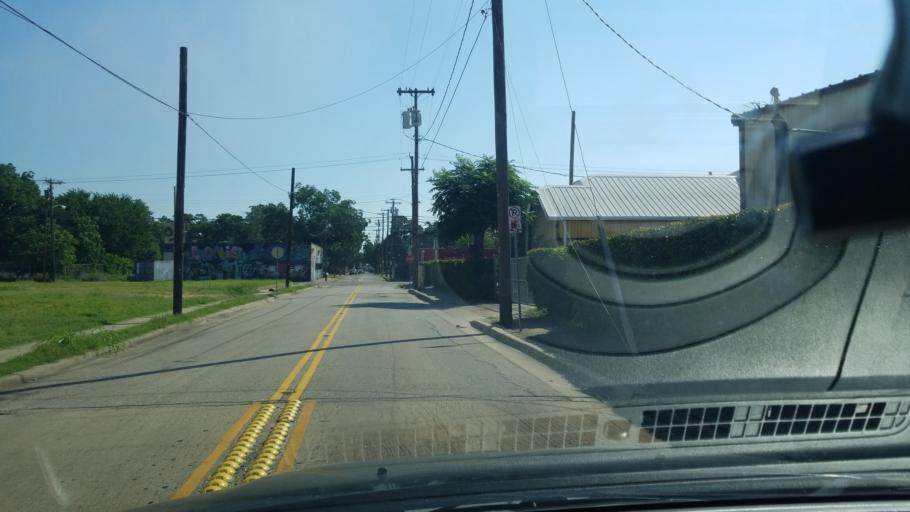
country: US
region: Texas
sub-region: Dallas County
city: Dallas
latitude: 32.7673
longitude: -96.7907
